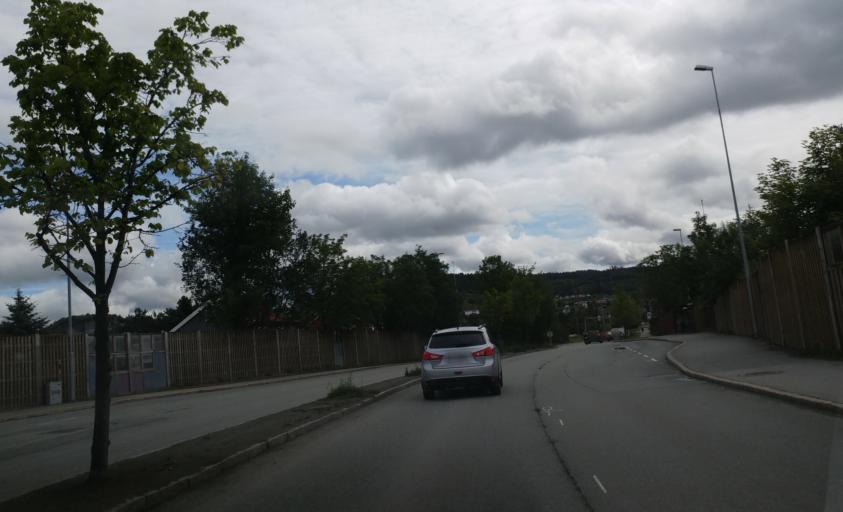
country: NO
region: Sor-Trondelag
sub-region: Trondheim
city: Trondheim
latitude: 63.4069
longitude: 10.4236
